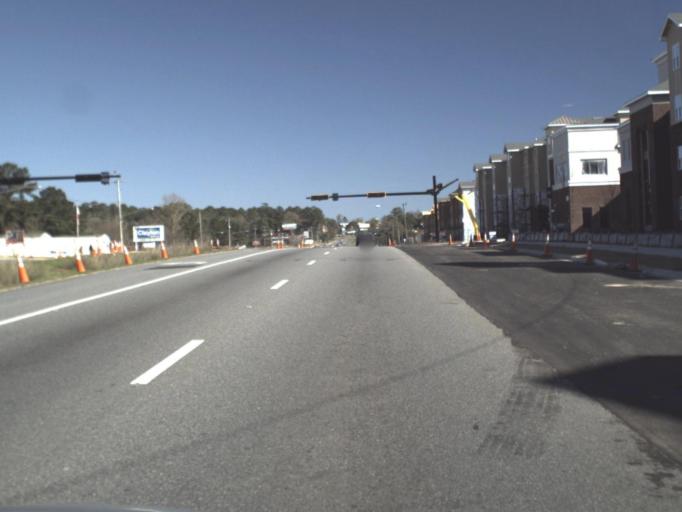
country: US
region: Florida
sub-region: Leon County
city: Tallahassee
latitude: 30.4504
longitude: -84.3330
